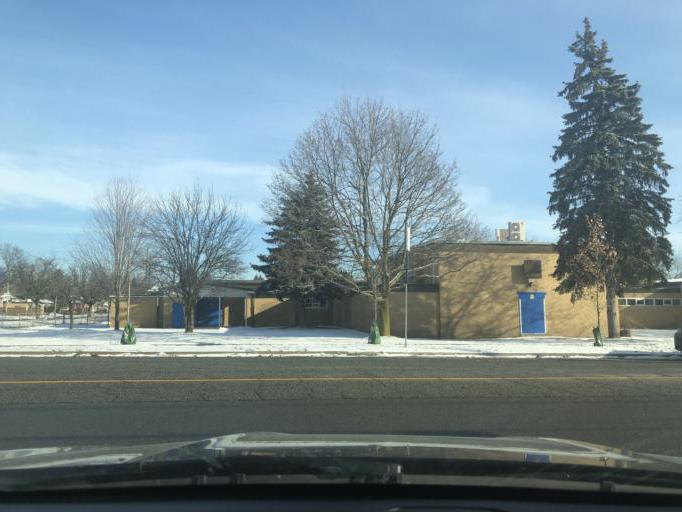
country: CA
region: Ontario
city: Scarborough
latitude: 43.7873
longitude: -79.1510
